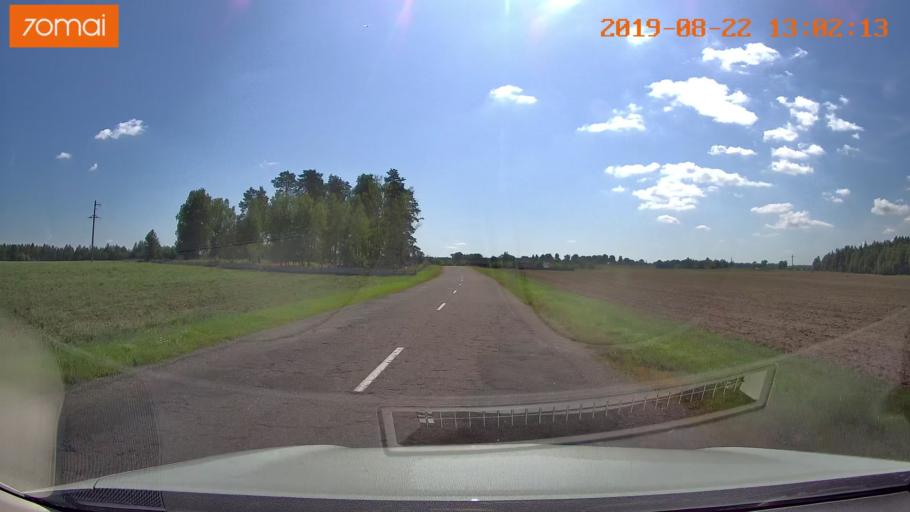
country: BY
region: Minsk
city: Prawdzinski
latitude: 53.3916
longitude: 27.8241
